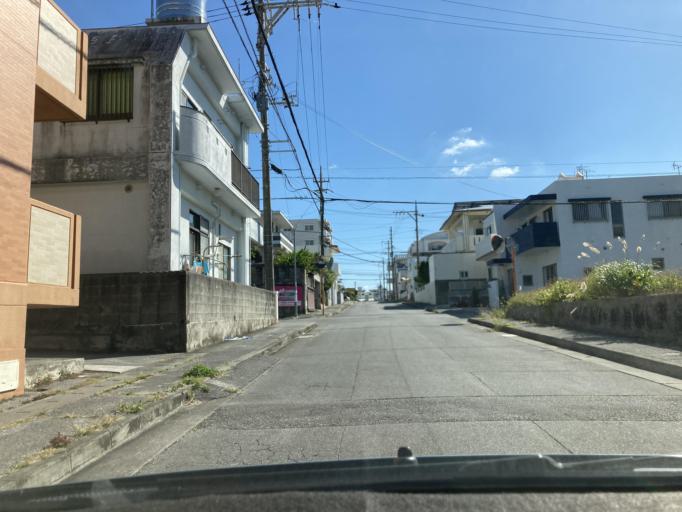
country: JP
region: Okinawa
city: Okinawa
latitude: 26.3457
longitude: 127.8278
